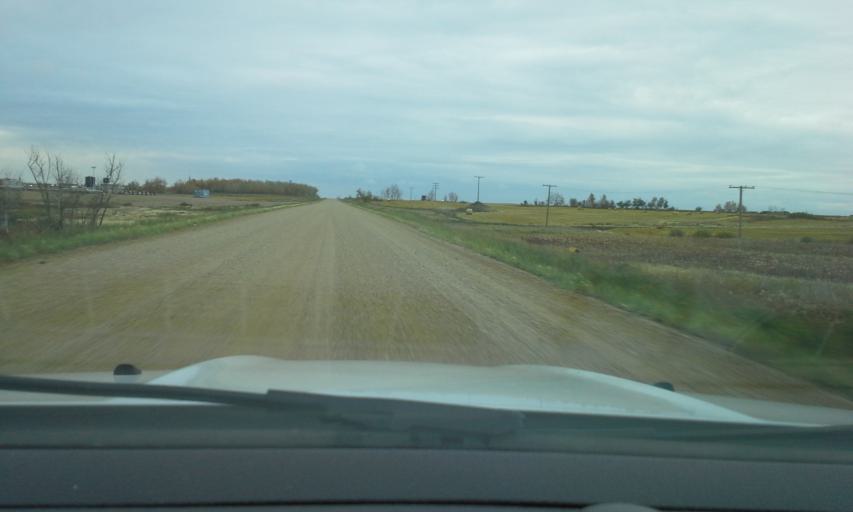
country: CA
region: Saskatchewan
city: Lloydminster
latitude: 53.2807
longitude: -109.8084
